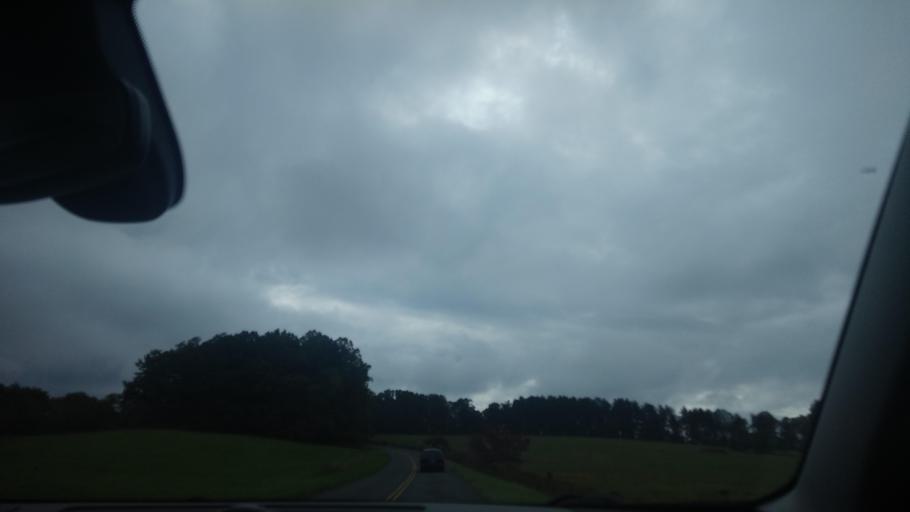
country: US
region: Virginia
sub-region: Carroll County
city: Cana
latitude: 36.6624
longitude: -80.6024
